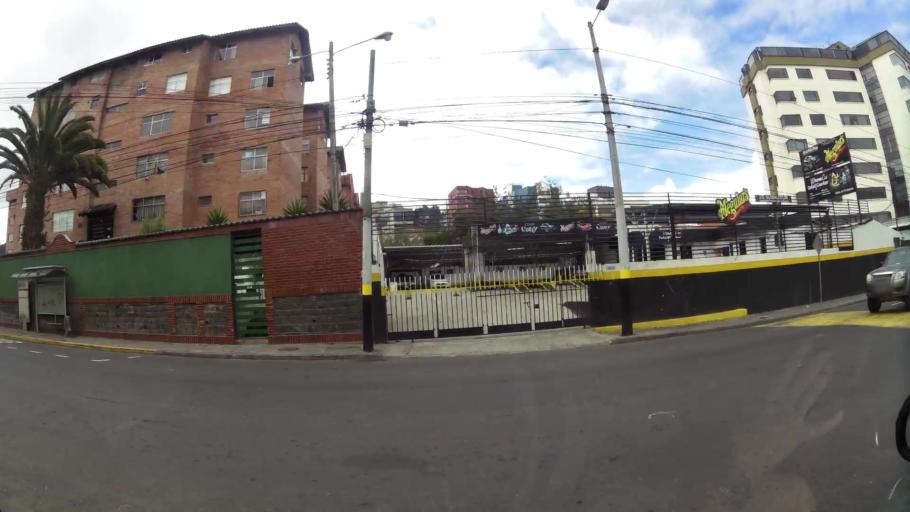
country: EC
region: Pichincha
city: Quito
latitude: -0.1669
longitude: -78.4703
